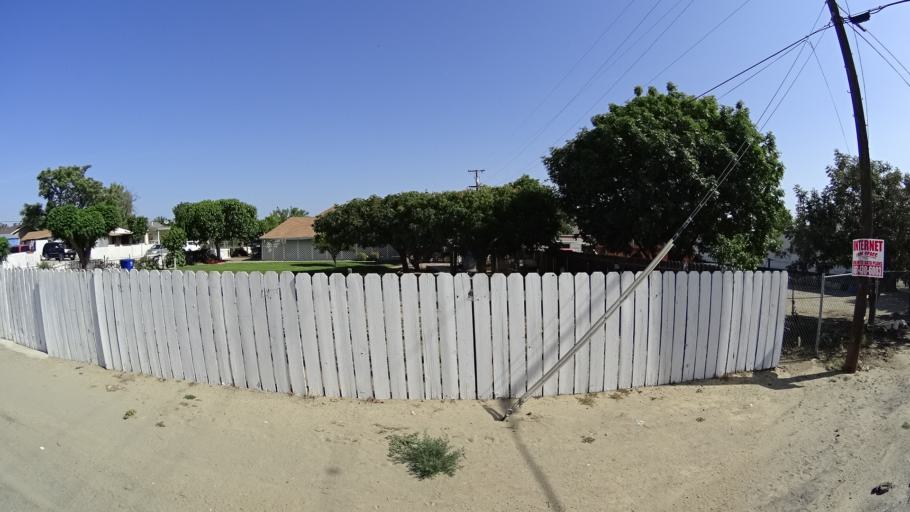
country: US
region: California
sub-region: Kings County
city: Kettleman City
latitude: 36.0093
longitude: -119.9637
